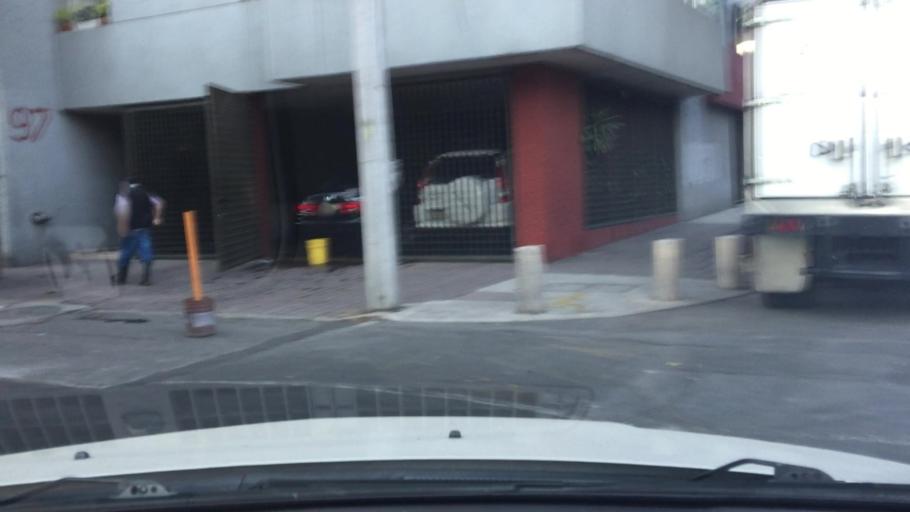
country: MX
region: Mexico City
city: Alvaro Obregon
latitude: 19.3647
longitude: -99.1900
